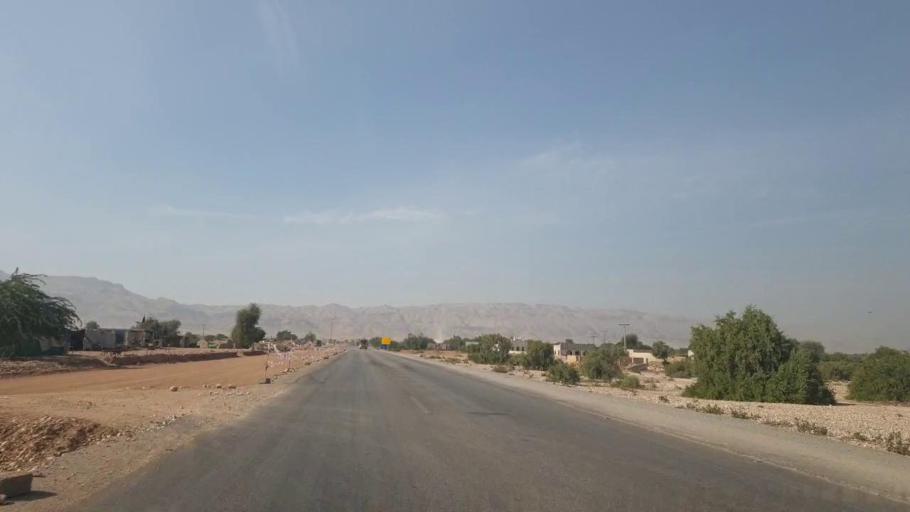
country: PK
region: Sindh
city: Sehwan
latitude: 26.2170
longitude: 67.9137
